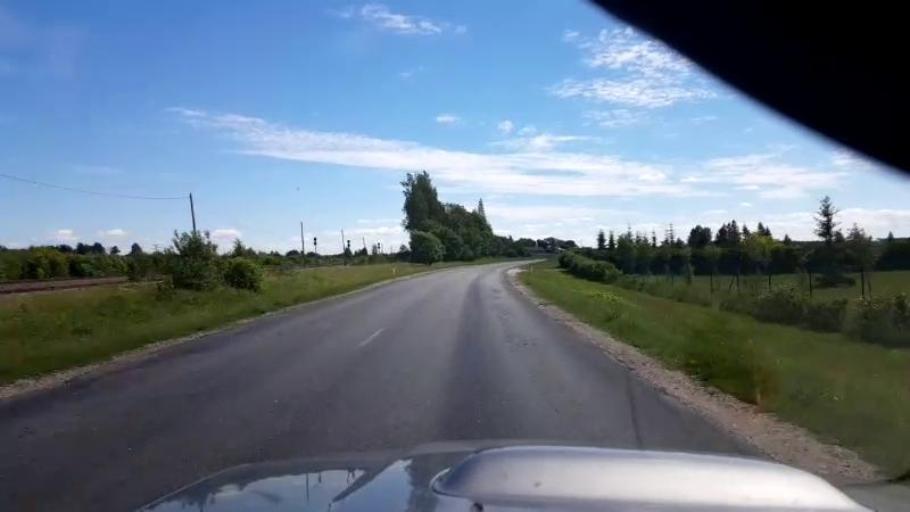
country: EE
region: Laeaene-Virumaa
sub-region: Rakke vald
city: Rakke
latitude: 58.9060
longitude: 26.2807
